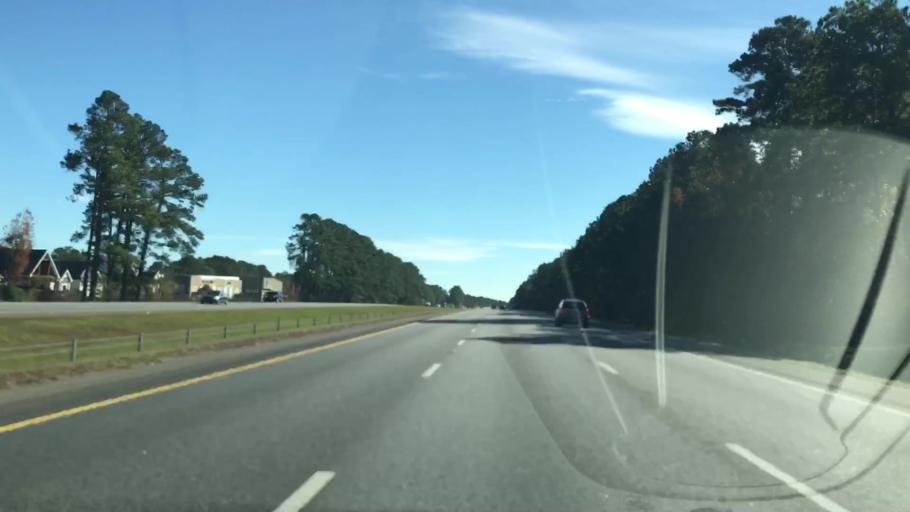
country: US
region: South Carolina
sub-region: Berkeley County
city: Sangaree
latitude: 33.0150
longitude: -80.1185
